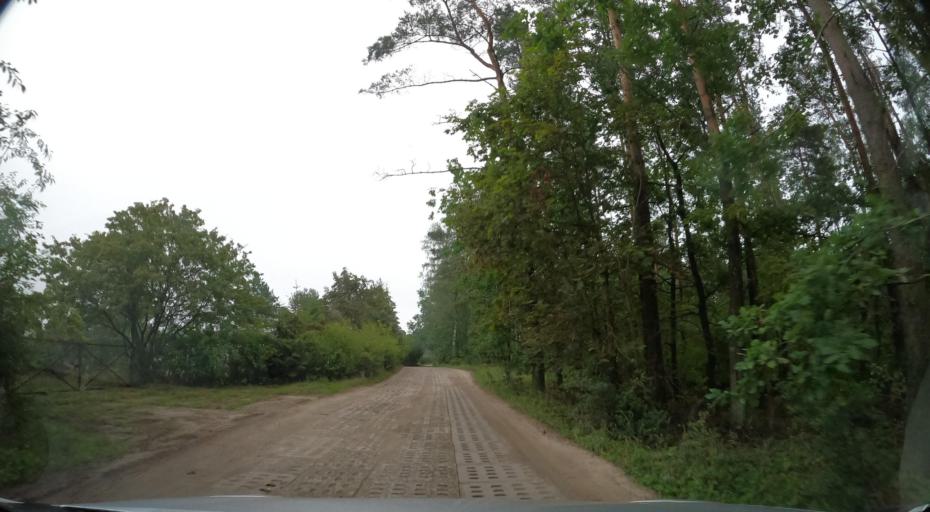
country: PL
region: Pomeranian Voivodeship
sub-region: Powiat kartuski
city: Chwaszczyno
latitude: 54.4212
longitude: 18.4188
